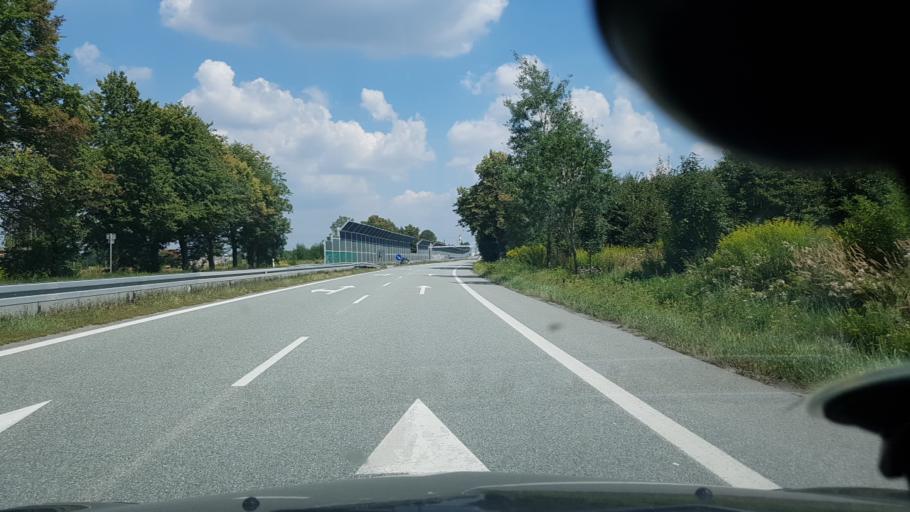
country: PL
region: Silesian Voivodeship
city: Gardawice
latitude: 50.1041
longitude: 18.7829
